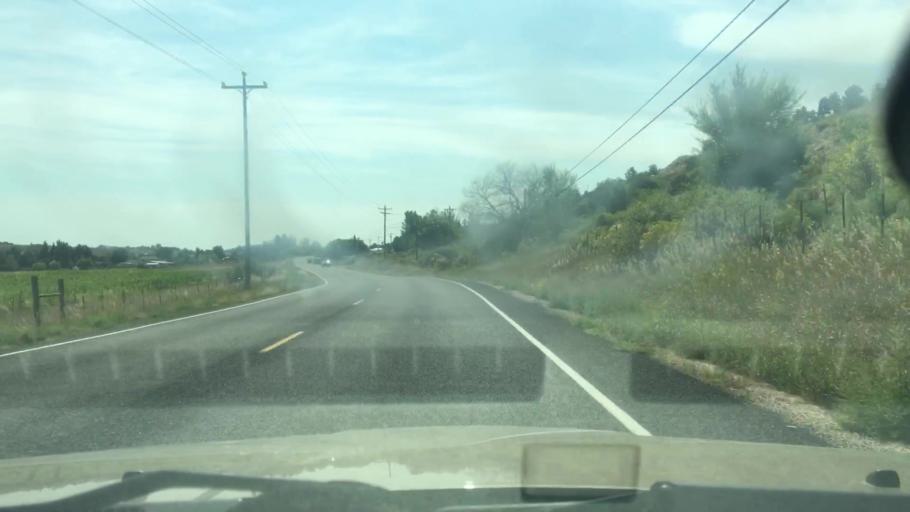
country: US
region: Colorado
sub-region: Larimer County
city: Loveland
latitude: 40.4442
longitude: -105.2017
